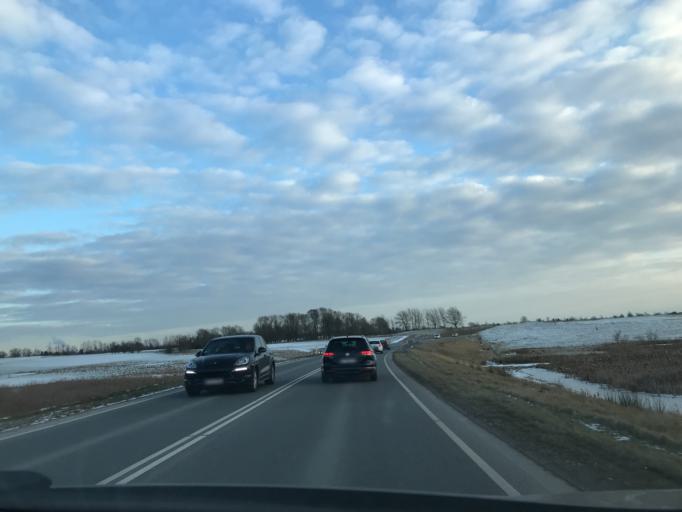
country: DK
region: Capital Region
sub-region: Egedal Kommune
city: Smorumnedre
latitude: 55.7274
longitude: 12.3119
